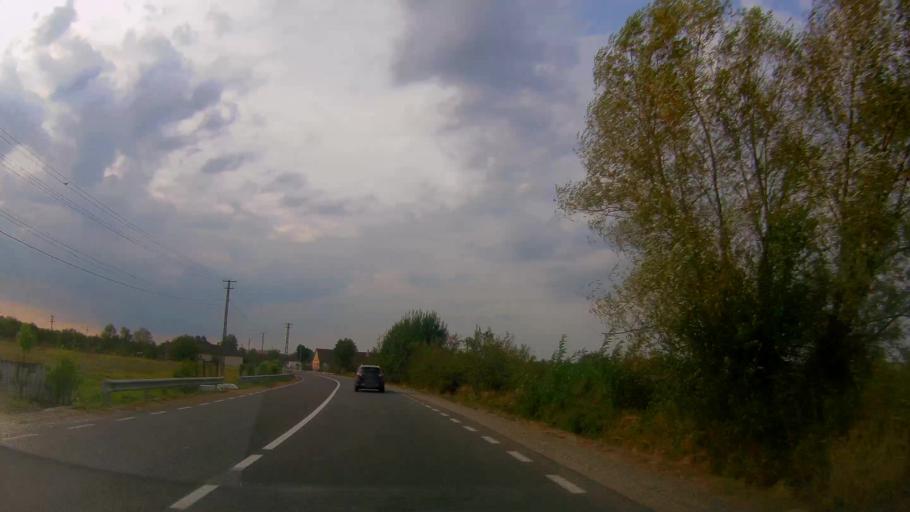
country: RO
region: Satu Mare
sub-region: Oras Ardud
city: Ardud
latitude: 47.5986
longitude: 22.8776
